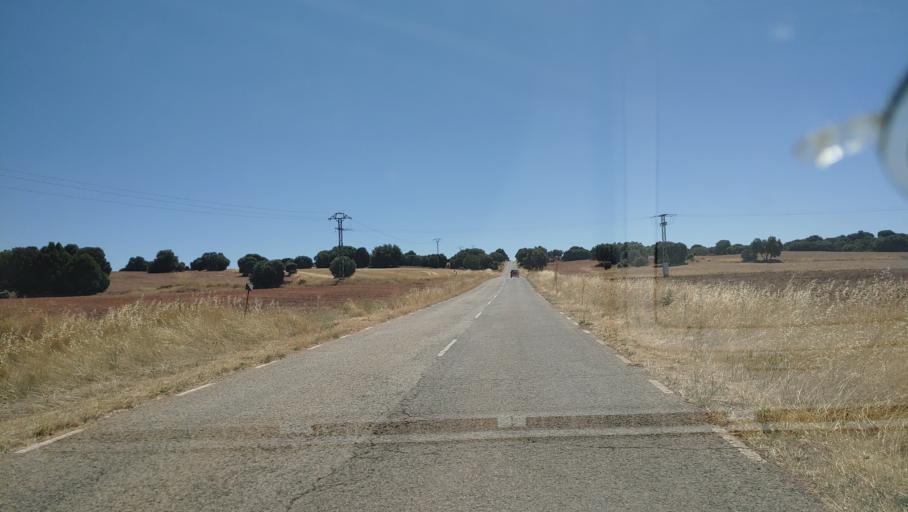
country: ES
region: Castille-La Mancha
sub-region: Provincia de Albacete
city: Ossa de Montiel
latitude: 38.9329
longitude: -2.7528
